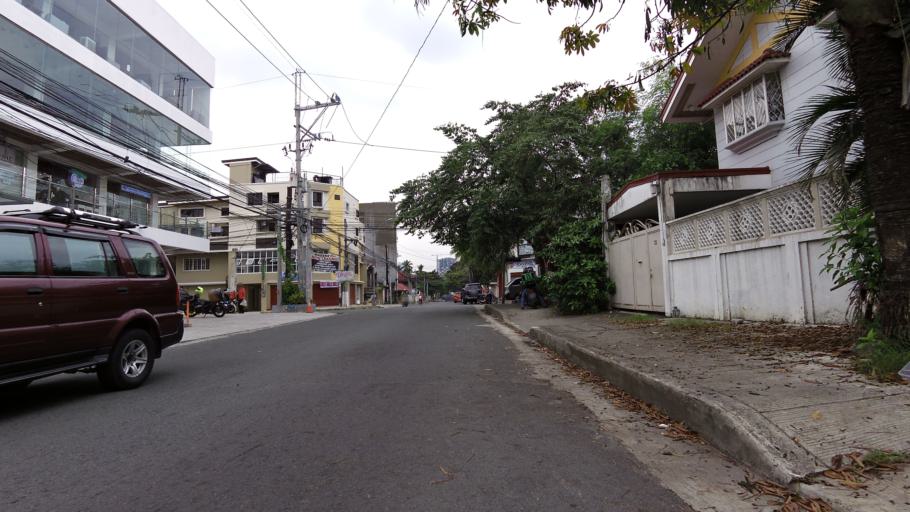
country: PH
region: Metro Manila
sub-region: Quezon City
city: Quezon City
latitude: 14.6394
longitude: 121.0568
